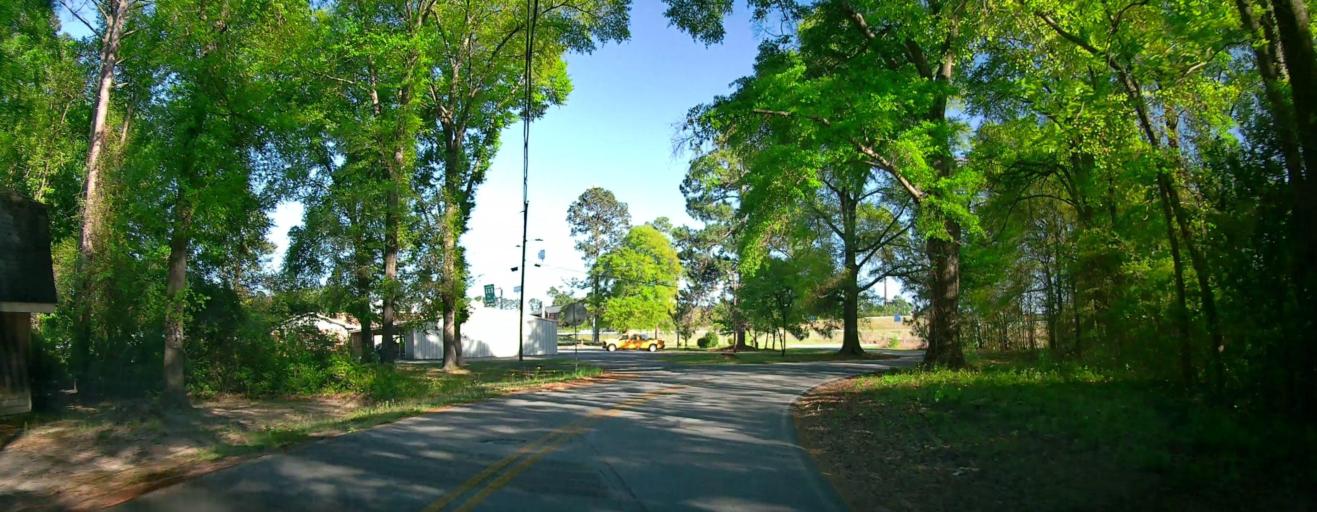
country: US
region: Georgia
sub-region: Houston County
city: Perry
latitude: 32.4503
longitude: -83.7559
